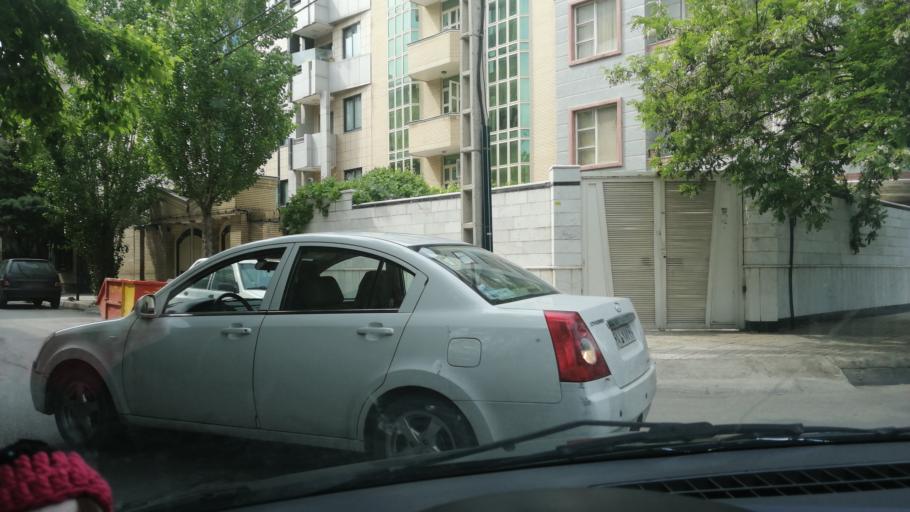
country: IR
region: Razavi Khorasan
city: Mashhad
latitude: 36.3264
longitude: 59.5669
